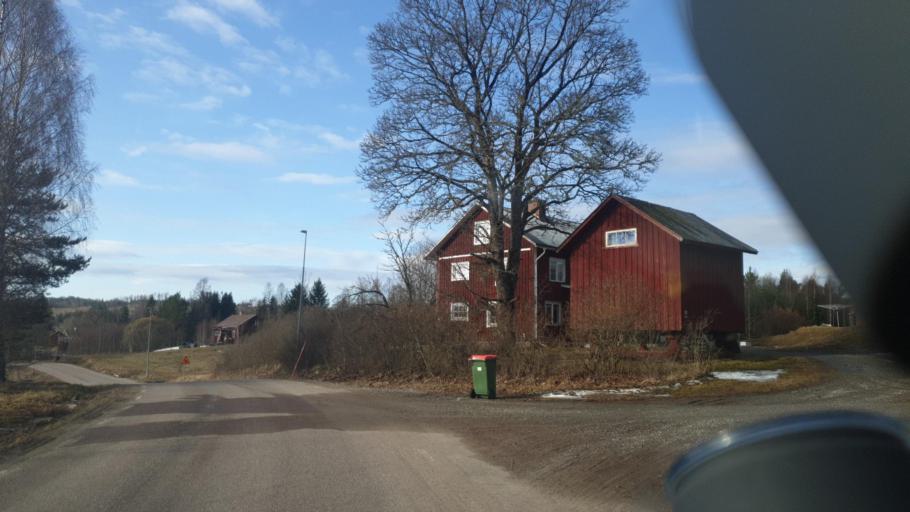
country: SE
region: Vaermland
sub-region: Arvika Kommun
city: Arvika
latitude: 59.7762
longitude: 12.8232
